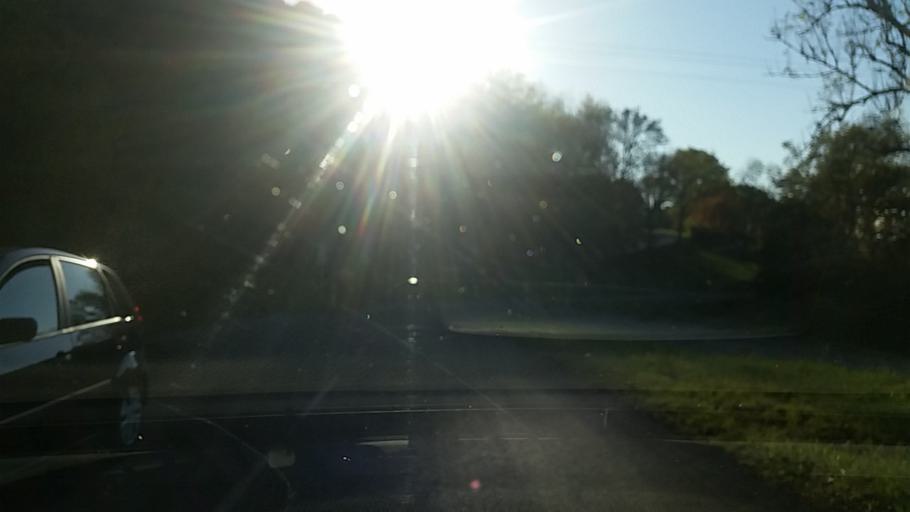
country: FR
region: Franche-Comte
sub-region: Departement du Doubs
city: Levier
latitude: 47.0013
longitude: 6.0300
